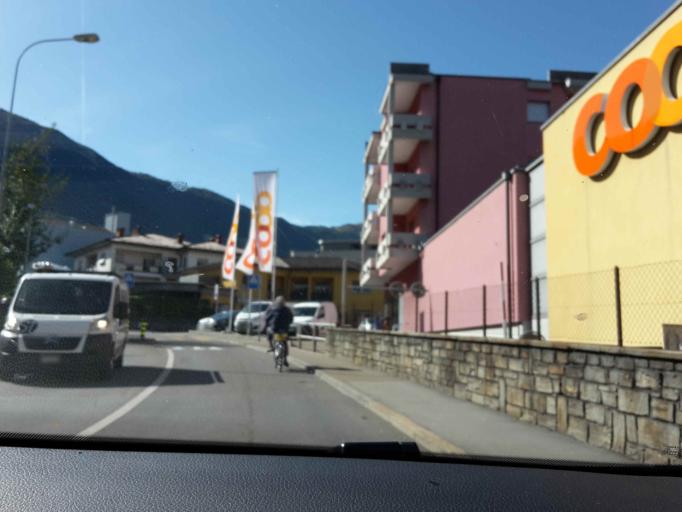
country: CH
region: Ticino
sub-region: Bellinzona District
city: Giubiasco
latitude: 46.1740
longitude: 9.0108
